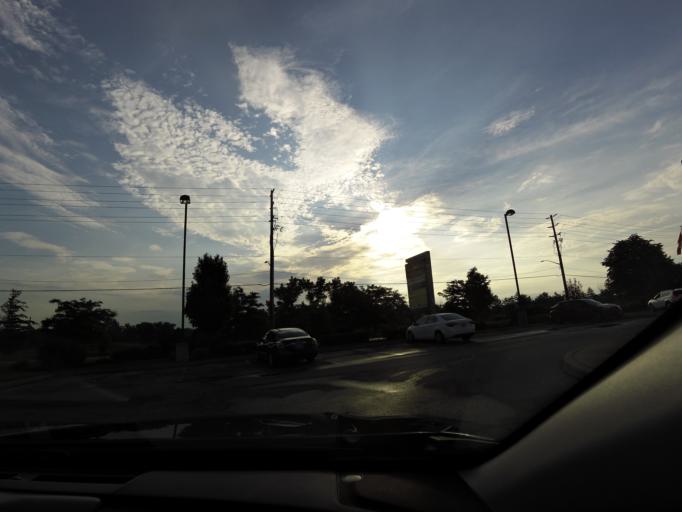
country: CA
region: Ontario
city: Burlington
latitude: 43.4007
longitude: -79.7648
